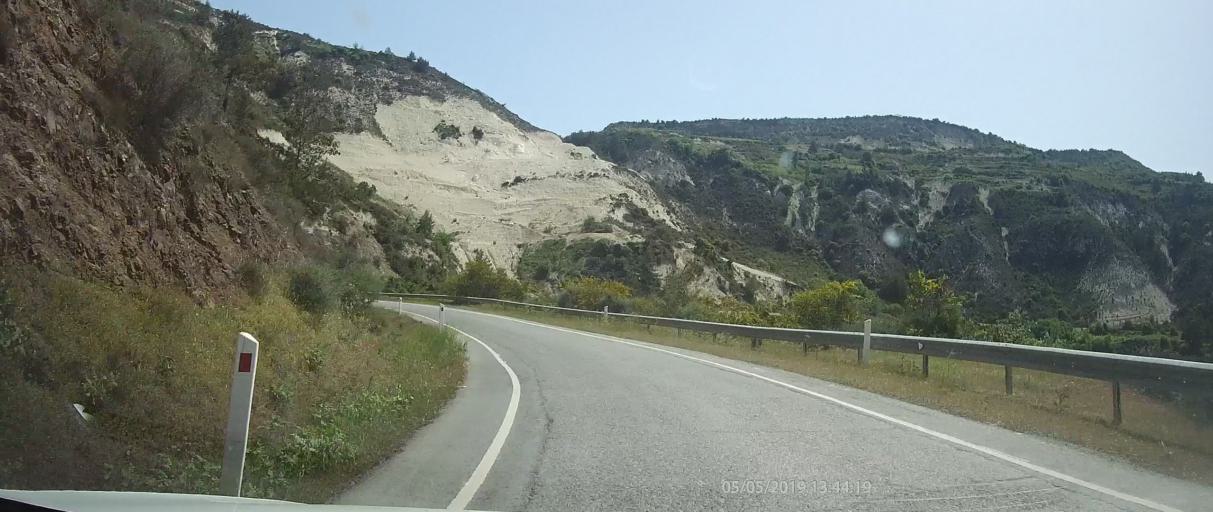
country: CY
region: Limassol
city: Pachna
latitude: 34.8709
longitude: 32.7909
